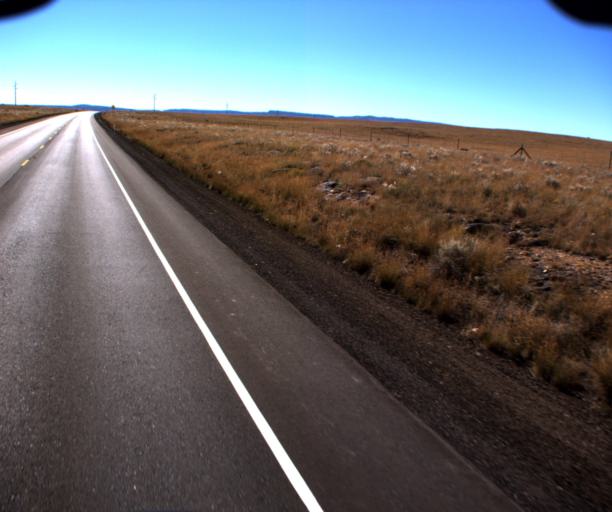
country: US
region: Arizona
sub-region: Apache County
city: Springerville
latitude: 34.1886
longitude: -109.3205
